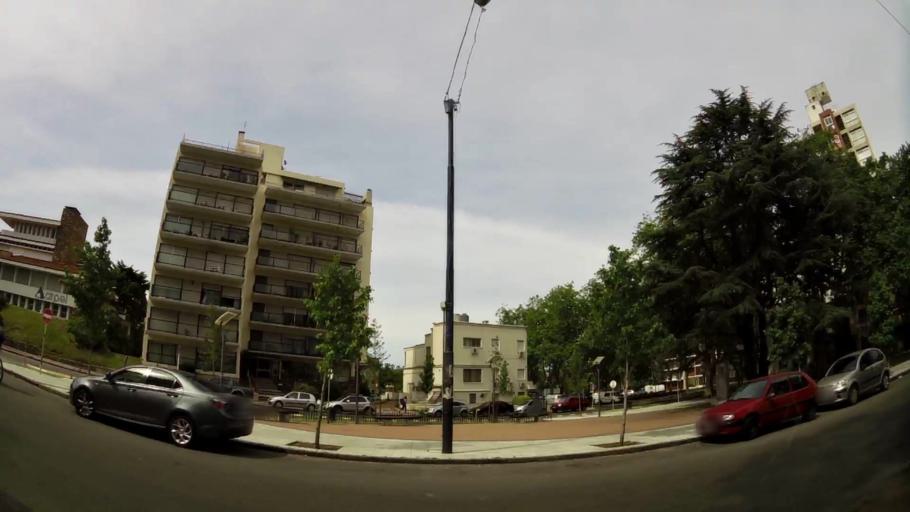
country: UY
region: Montevideo
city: Montevideo
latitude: -34.9103
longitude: -56.1652
